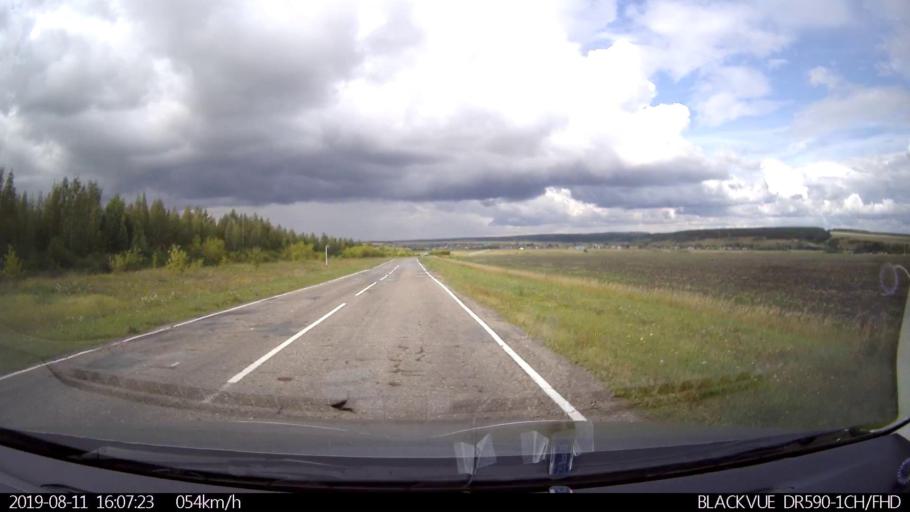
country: RU
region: Ulyanovsk
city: Ignatovka
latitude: 53.9766
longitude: 47.6465
